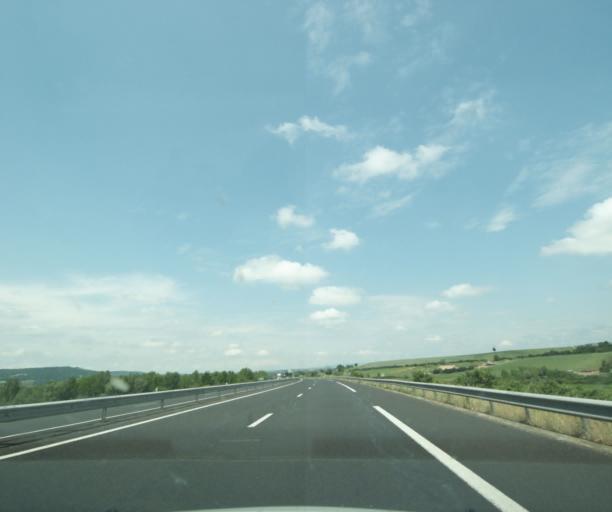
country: FR
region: Auvergne
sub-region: Departement de la Haute-Loire
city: Lempdes-sur-Allagnon
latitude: 45.3709
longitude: 3.2866
